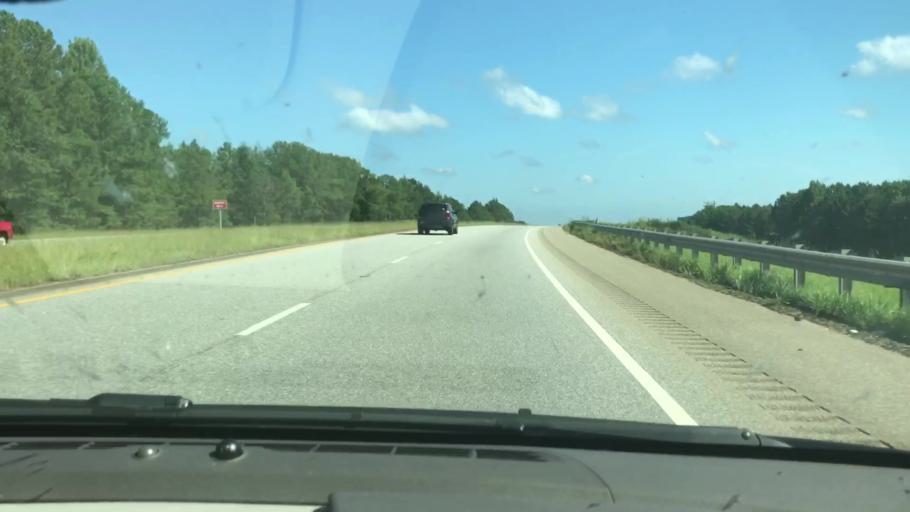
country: US
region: Alabama
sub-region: Barbour County
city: Eufaula
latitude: 32.1586
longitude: -85.1782
